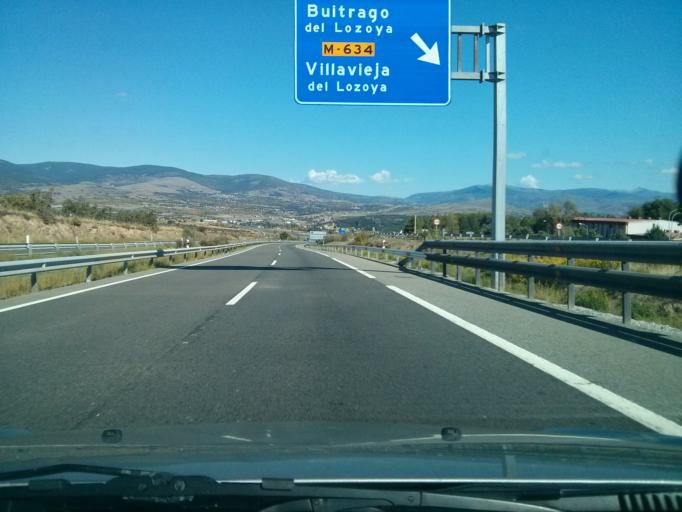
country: ES
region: Madrid
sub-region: Provincia de Madrid
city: Buitrago del Lozoya
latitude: 40.9713
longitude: -3.6400
